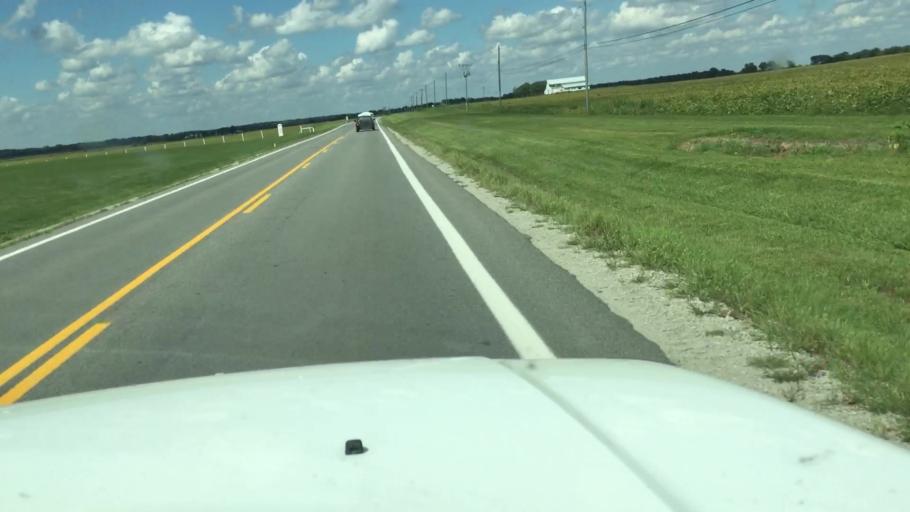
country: US
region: Ohio
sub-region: Madison County
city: London
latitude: 39.9127
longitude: -83.4766
